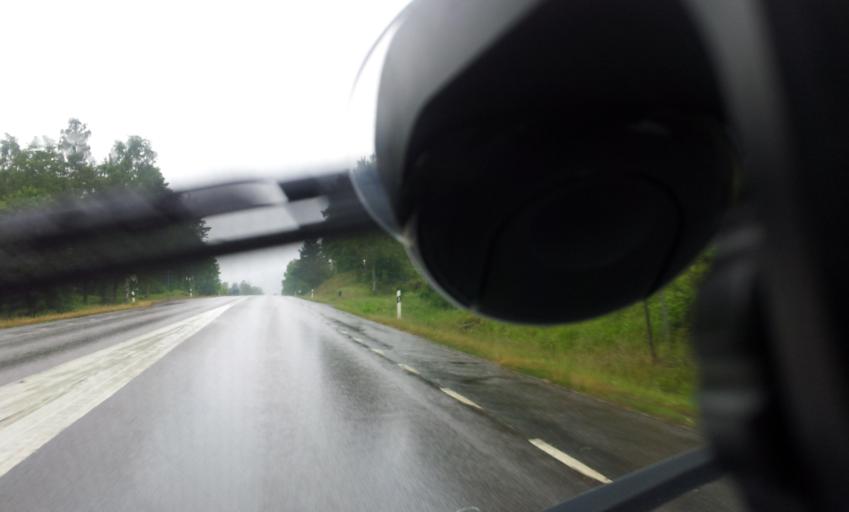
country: SE
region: Kalmar
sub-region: Oskarshamns Kommun
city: Oskarshamn
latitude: 57.4949
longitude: 16.5128
